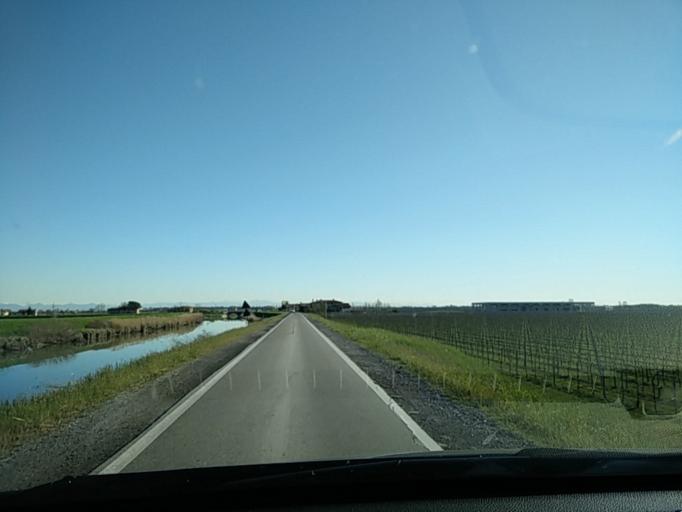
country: IT
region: Veneto
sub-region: Provincia di Venezia
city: San Dona di Piave
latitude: 45.6699
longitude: 12.5897
